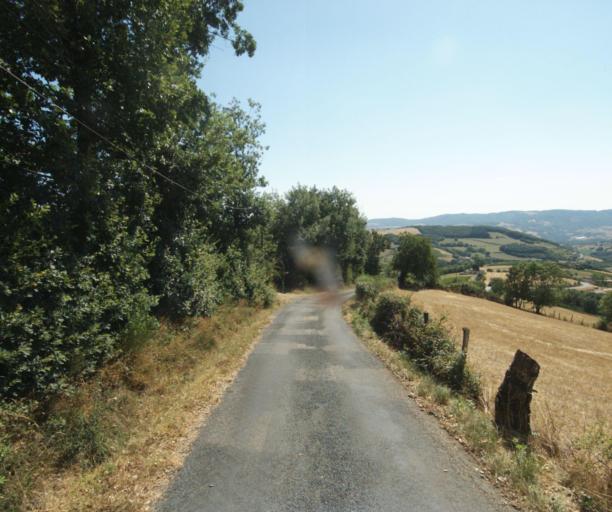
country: FR
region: Rhone-Alpes
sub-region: Departement du Rhone
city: Montrottier
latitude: 45.8037
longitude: 4.5100
